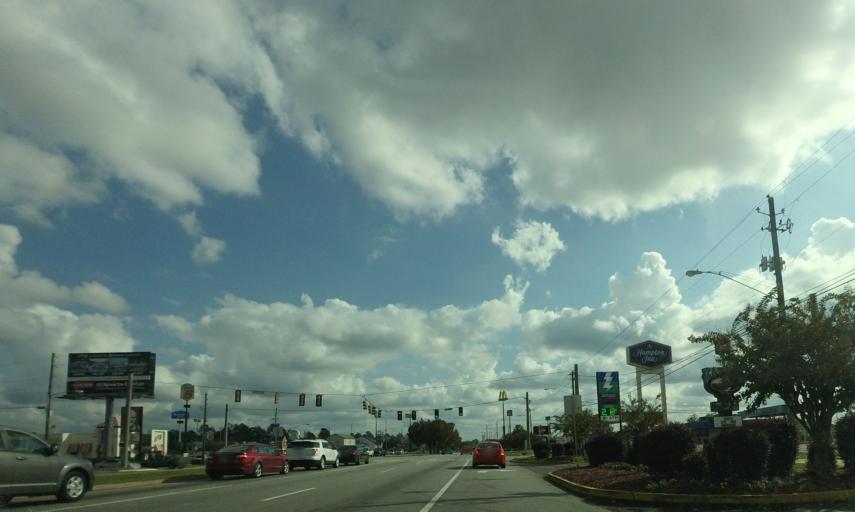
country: US
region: Georgia
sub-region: Houston County
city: Perry
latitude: 32.4701
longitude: -83.7426
